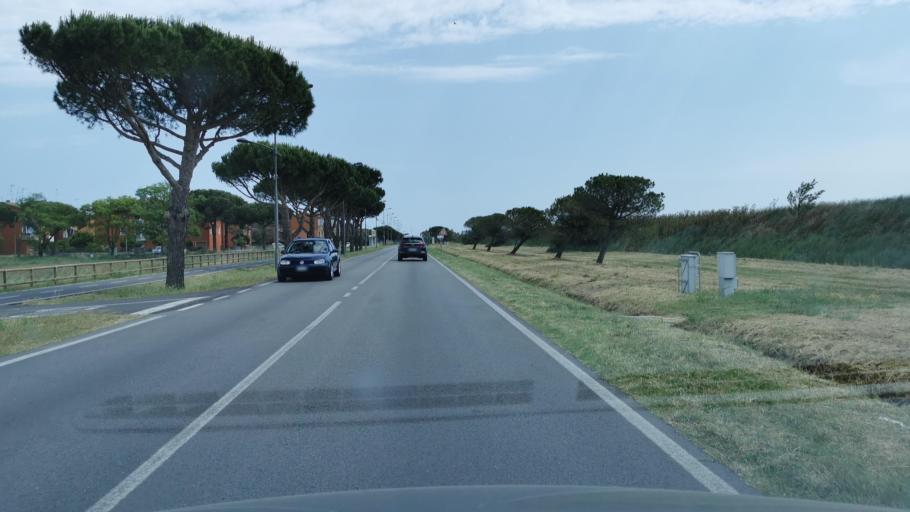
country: IT
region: Emilia-Romagna
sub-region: Provincia di Ferrara
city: Comacchio
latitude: 44.6874
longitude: 12.1917
